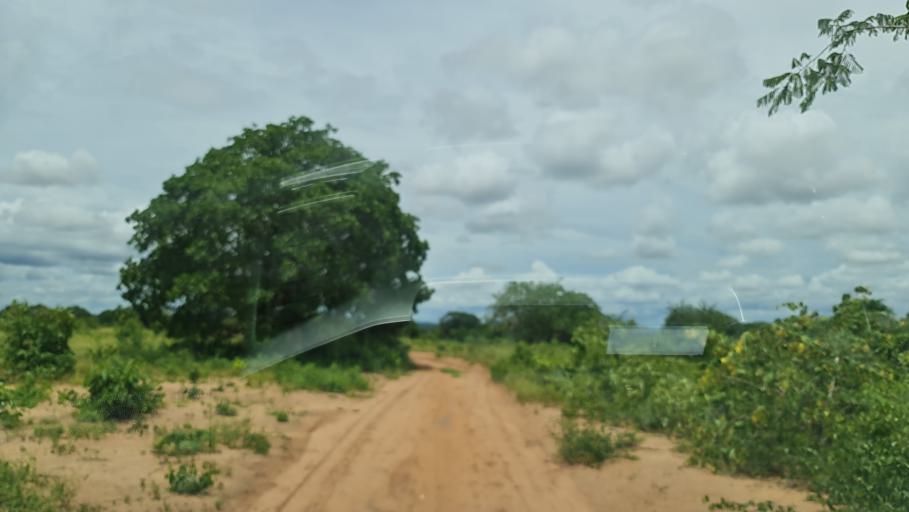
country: MZ
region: Nampula
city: Nacala
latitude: -14.7896
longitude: 39.9705
